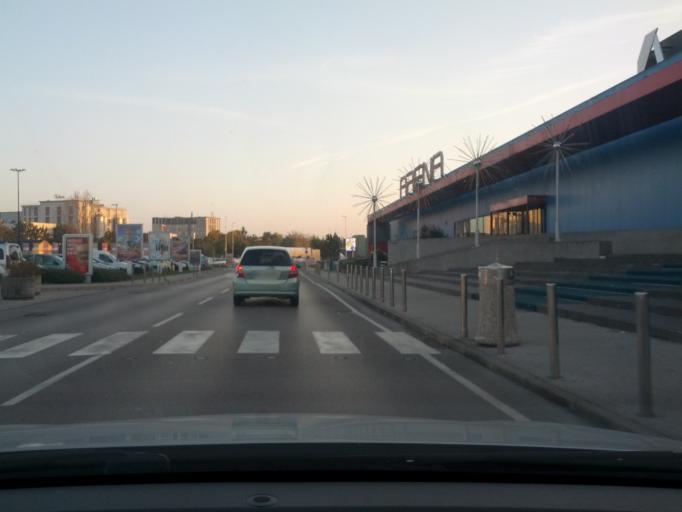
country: SI
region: Ljubljana
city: Ljubljana
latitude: 46.0655
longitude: 14.5485
